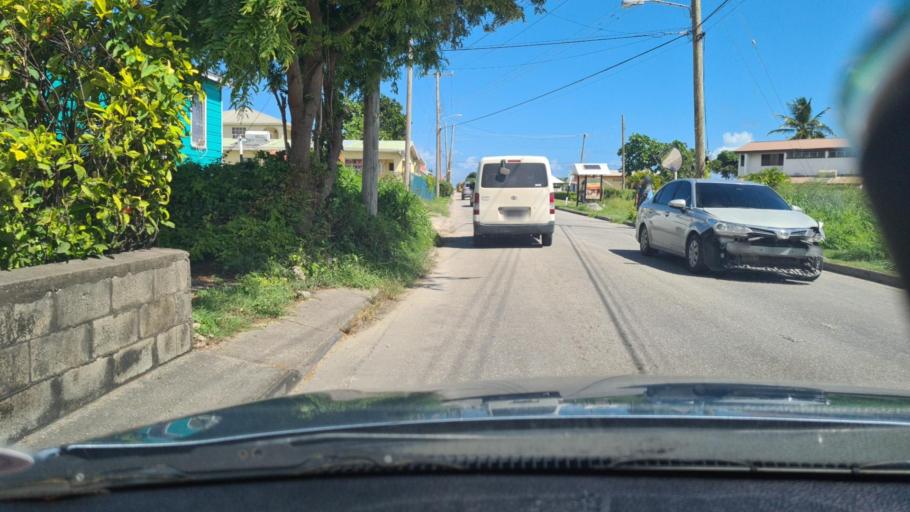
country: BB
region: Saint Philip
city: Crane
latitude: 13.1223
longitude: -59.4517
